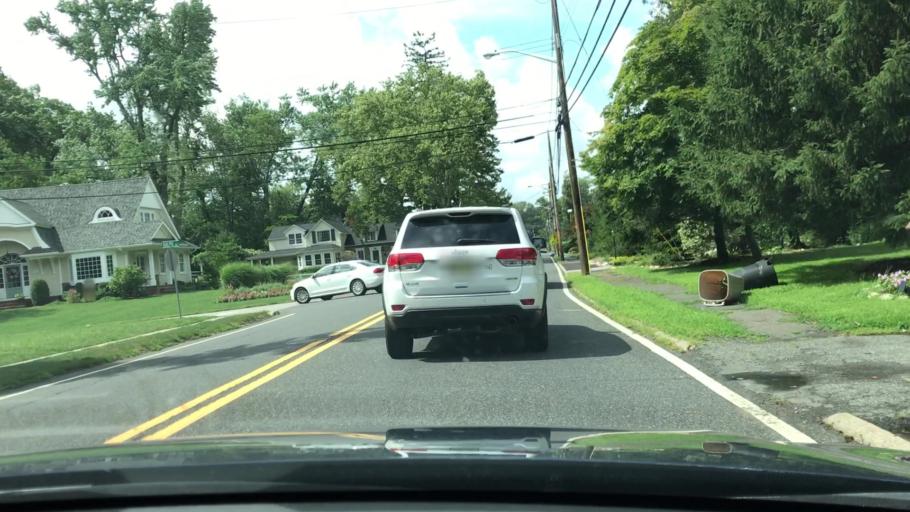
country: US
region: New Jersey
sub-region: Bergen County
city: Wyckoff
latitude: 41.0039
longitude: -74.1586
